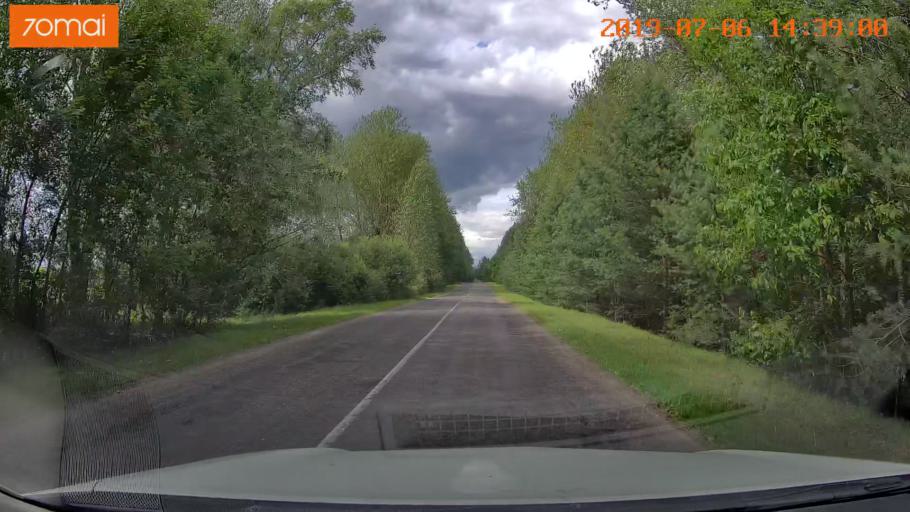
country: BY
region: Minsk
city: Ivyanyets
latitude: 53.9121
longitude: 26.6950
